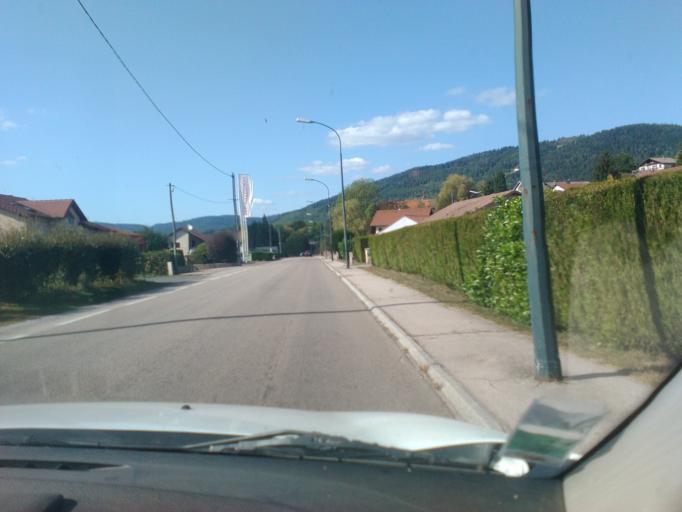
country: FR
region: Lorraine
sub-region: Departement des Vosges
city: Vagney
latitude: 48.0144
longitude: 6.7132
